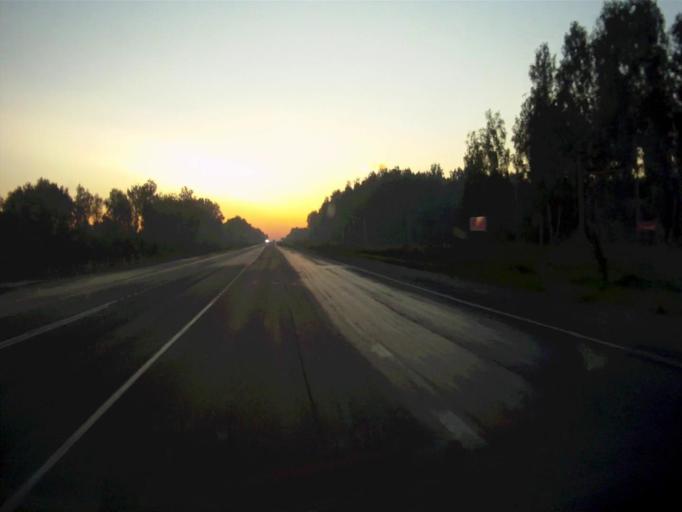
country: RU
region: Chelyabinsk
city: Poletayevo
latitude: 55.2070
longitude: 61.1020
